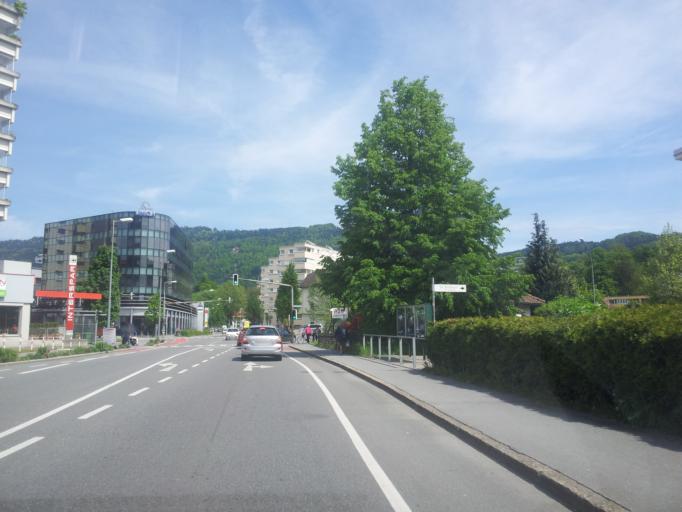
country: AT
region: Vorarlberg
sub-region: Politischer Bezirk Bregenz
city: Lauterach
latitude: 47.4973
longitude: 9.7281
